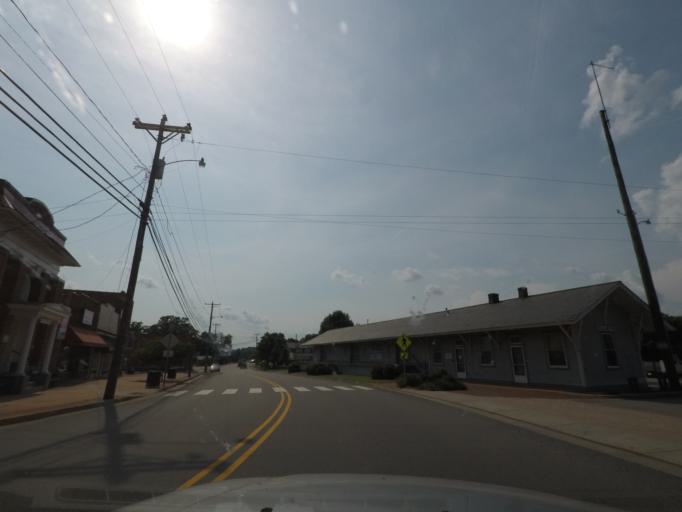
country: US
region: Virginia
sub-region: Buckingham County
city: Buckingham
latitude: 37.5425
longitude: -78.4568
